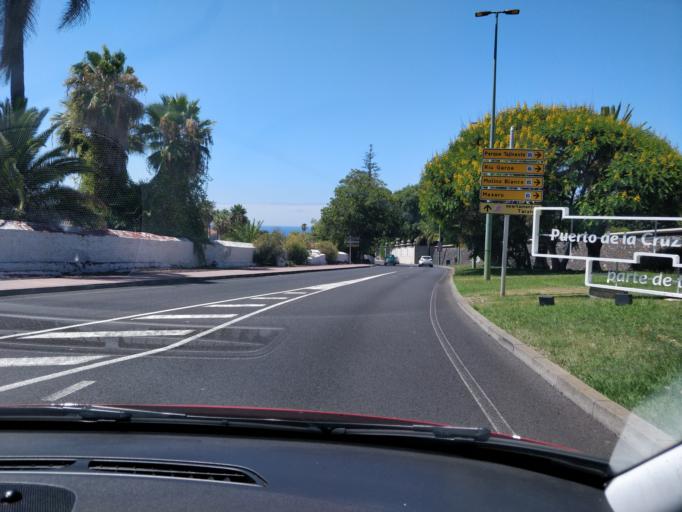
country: ES
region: Canary Islands
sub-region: Provincia de Santa Cruz de Tenerife
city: Puerto de la Cruz
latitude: 28.4089
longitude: -16.5348
